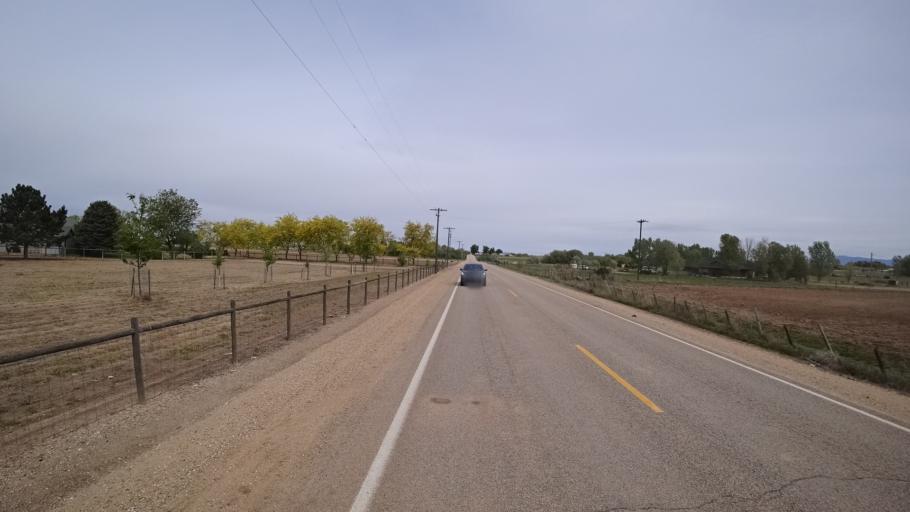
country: US
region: Idaho
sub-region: Ada County
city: Kuna
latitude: 43.5536
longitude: -116.4737
